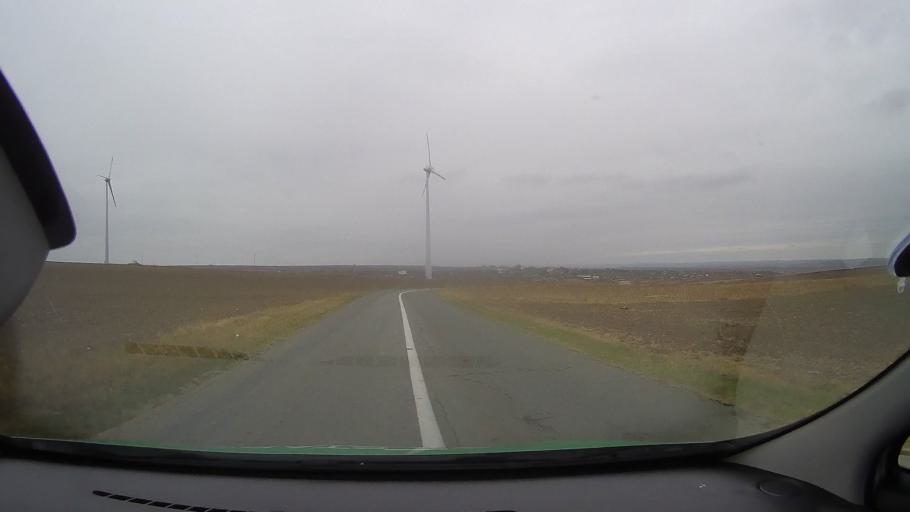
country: RO
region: Constanta
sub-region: Comuna Pantelimon
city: Pantelimon
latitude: 44.5338
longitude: 28.3263
